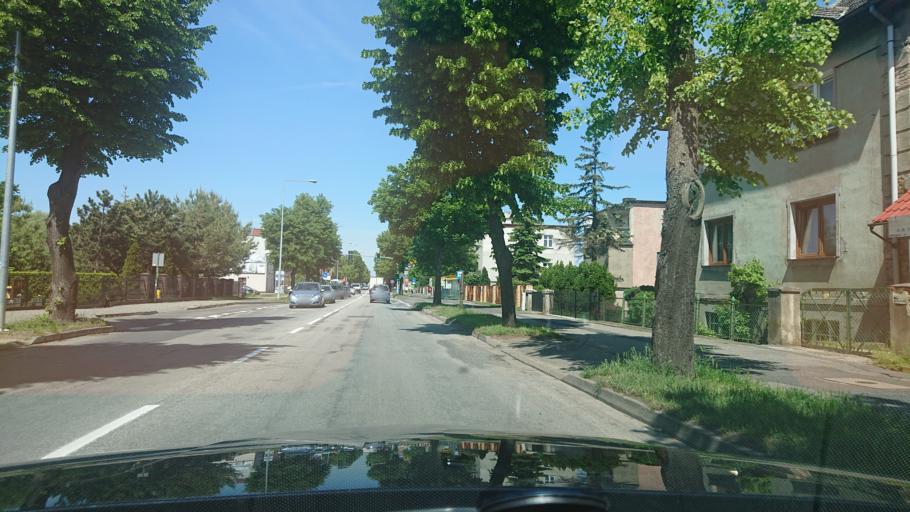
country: PL
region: Greater Poland Voivodeship
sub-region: Powiat gnieznienski
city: Gniezno
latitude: 52.5235
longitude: 17.6019
